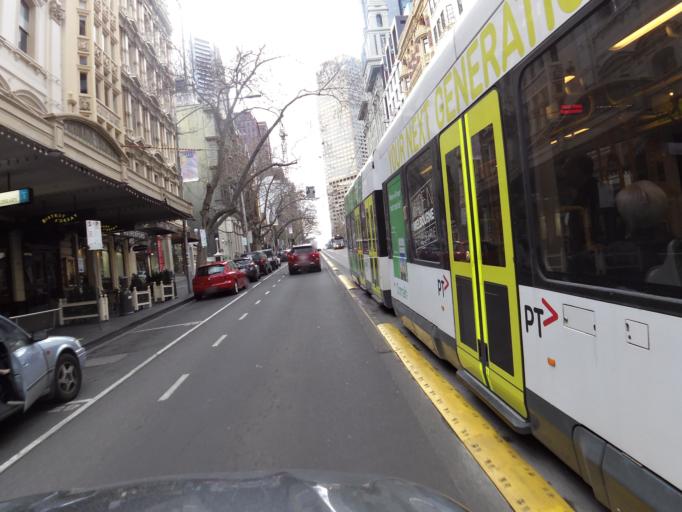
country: AU
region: Victoria
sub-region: Melbourne
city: Melbourne
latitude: -37.8152
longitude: 144.9672
